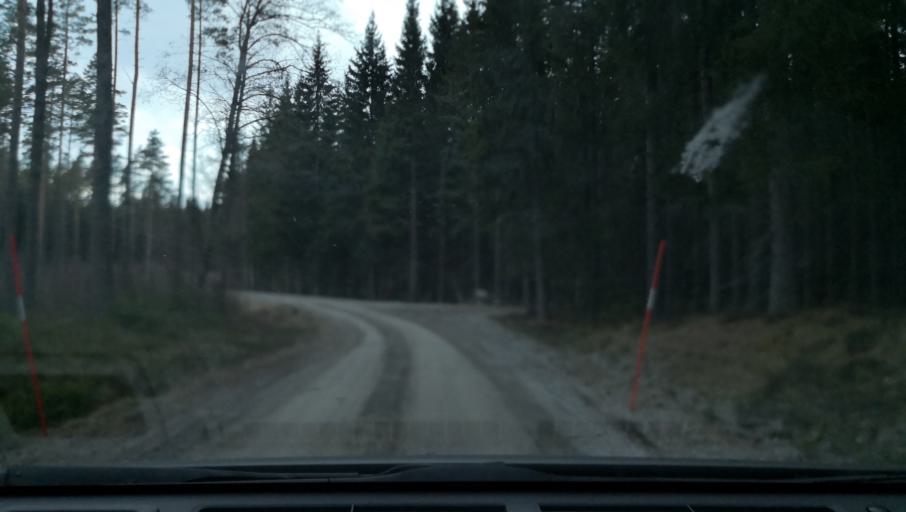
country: SE
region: Vaestmanland
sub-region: Kopings Kommun
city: Kolsva
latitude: 59.5590
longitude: 15.8582
